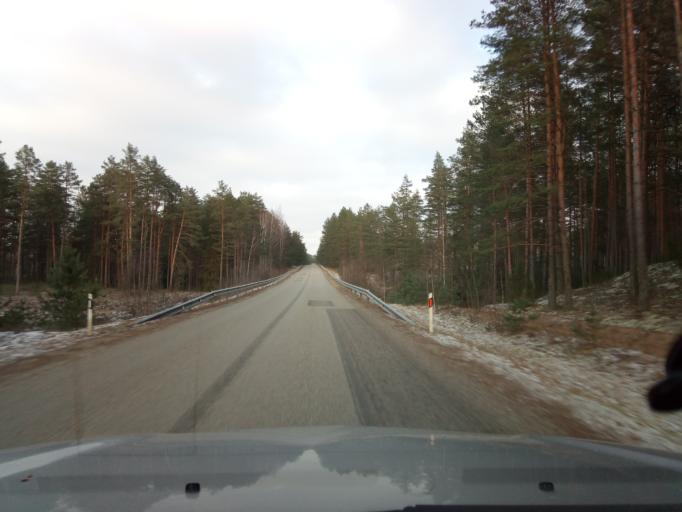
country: LT
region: Alytaus apskritis
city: Varena
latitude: 54.1863
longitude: 24.5201
